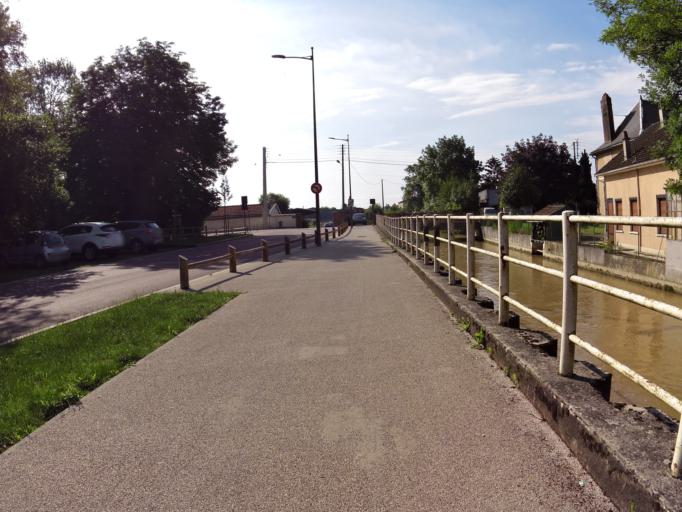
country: FR
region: Champagne-Ardenne
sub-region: Departement de l'Aube
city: Troyes
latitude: 48.2867
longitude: 4.0869
